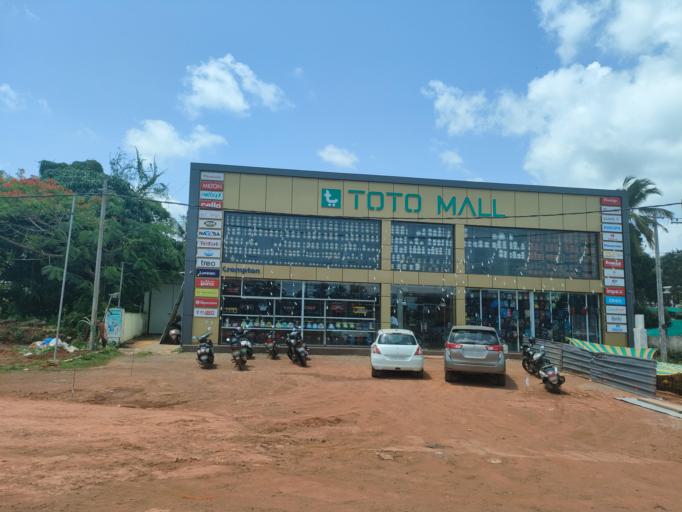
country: IN
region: Kerala
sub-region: Kasaragod District
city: Kasaragod
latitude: 12.5141
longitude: 75.0254
